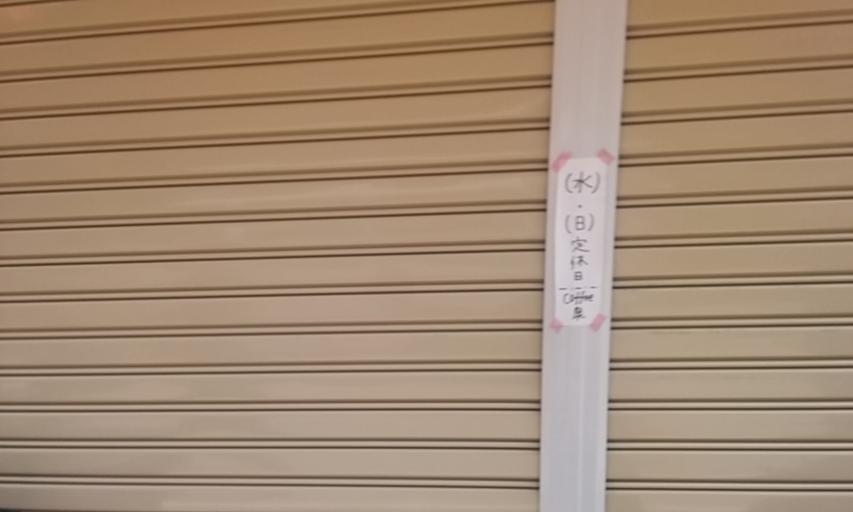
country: JP
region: Tokyo
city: Urayasu
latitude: 35.7017
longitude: 139.8487
